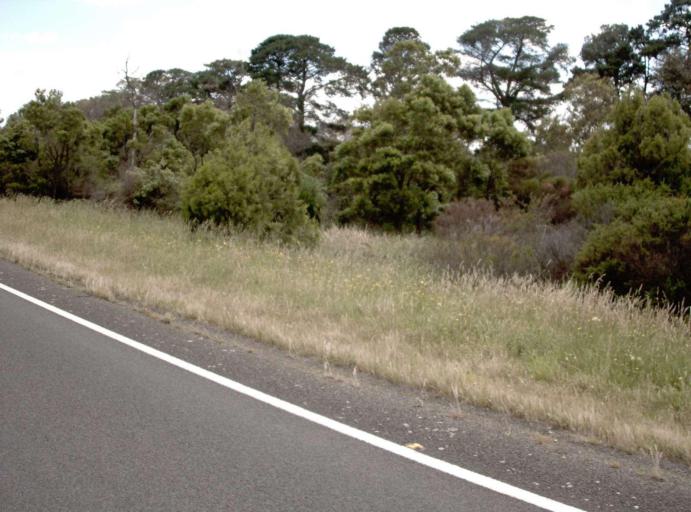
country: AU
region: Victoria
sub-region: Cardinia
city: Koo-Wee-Rup
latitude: -38.3007
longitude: 145.5431
